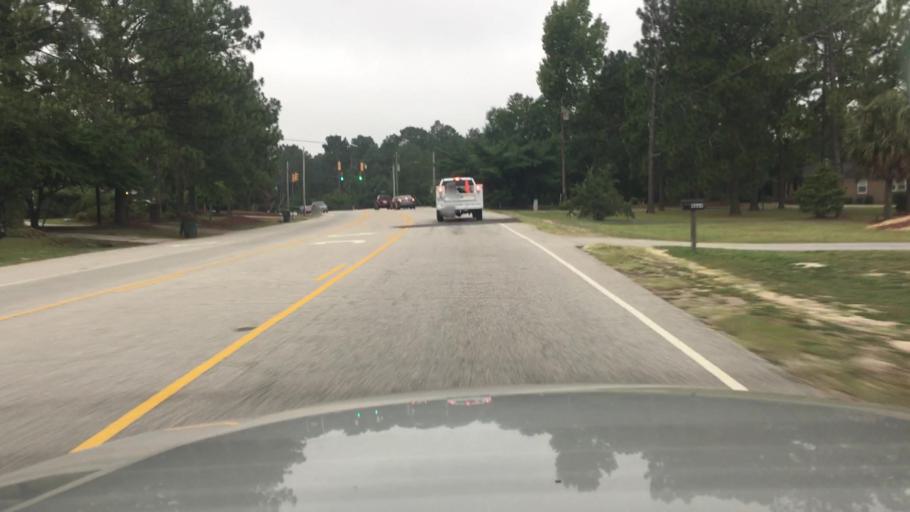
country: US
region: North Carolina
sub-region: Cumberland County
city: Hope Mills
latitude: 34.9762
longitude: -78.9385
